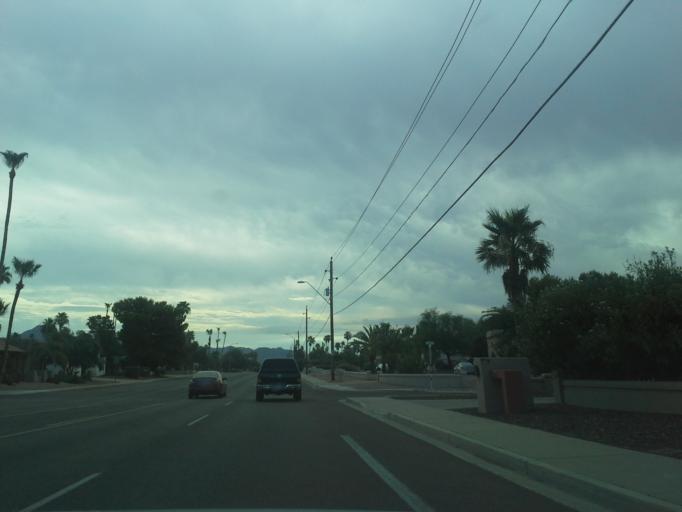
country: US
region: Arizona
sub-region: Maricopa County
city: Paradise Valley
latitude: 33.6112
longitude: -111.9328
